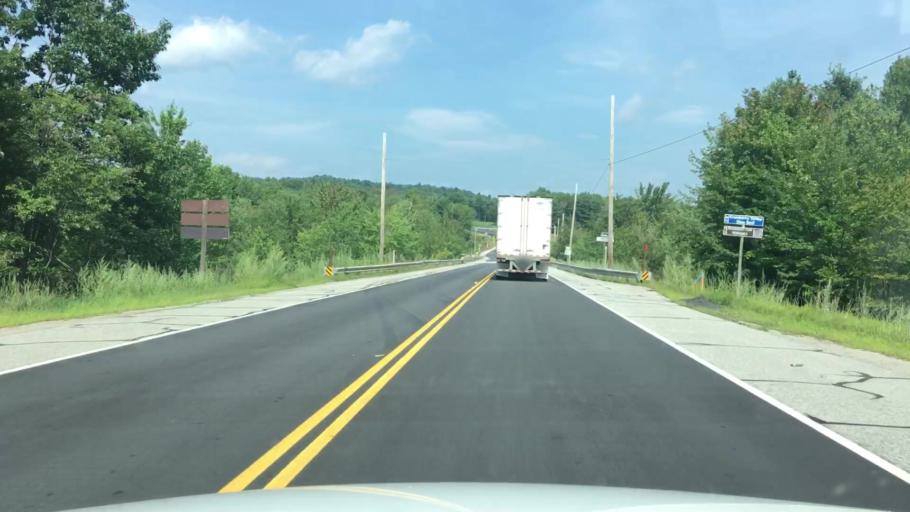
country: US
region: Maine
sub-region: Androscoggin County
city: Turner
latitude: 44.2542
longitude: -70.2592
